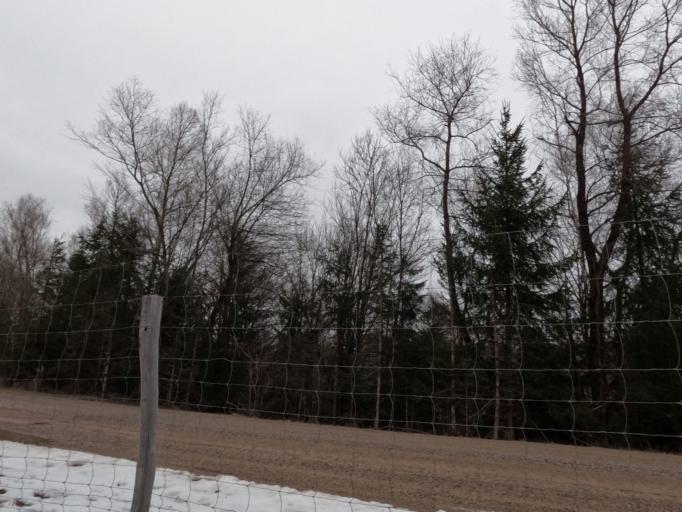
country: DE
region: Bavaria
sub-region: Upper Bavaria
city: Vachendorf
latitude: 47.8590
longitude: 12.5831
